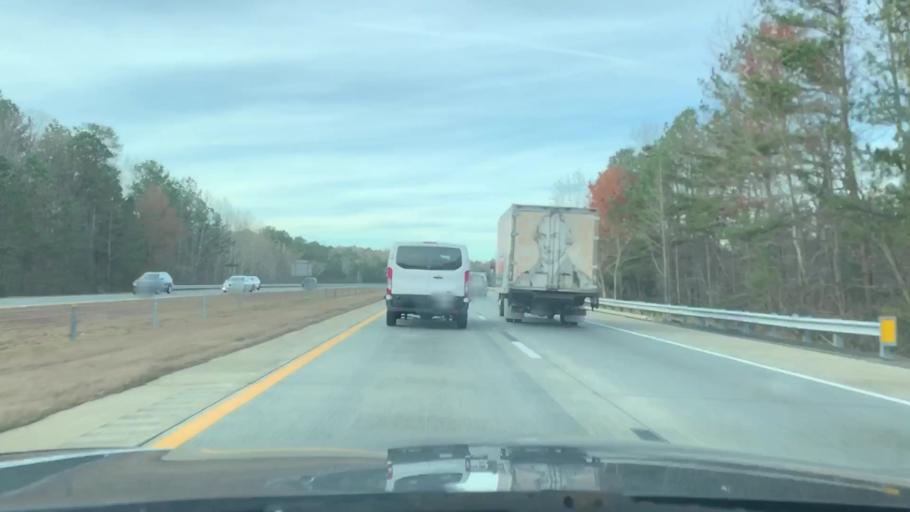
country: US
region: North Carolina
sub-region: Orange County
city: Chapel Hill
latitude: 35.9838
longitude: -79.0737
